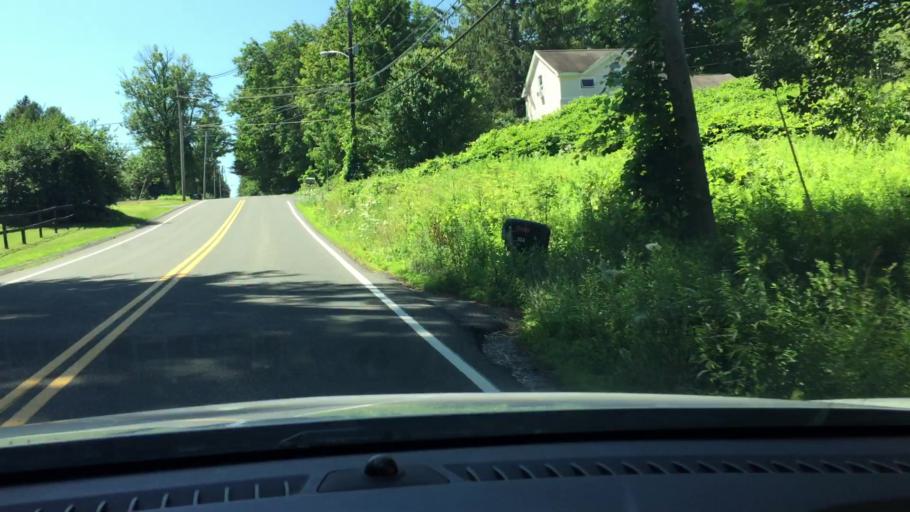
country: US
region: Massachusetts
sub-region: Berkshire County
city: Lenox
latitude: 42.3621
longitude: -73.2595
